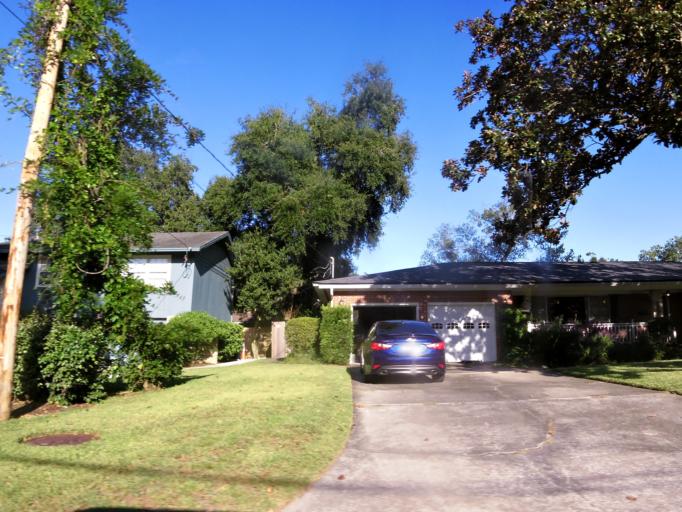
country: US
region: Florida
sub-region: Duval County
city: Jacksonville
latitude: 30.2490
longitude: -81.6279
